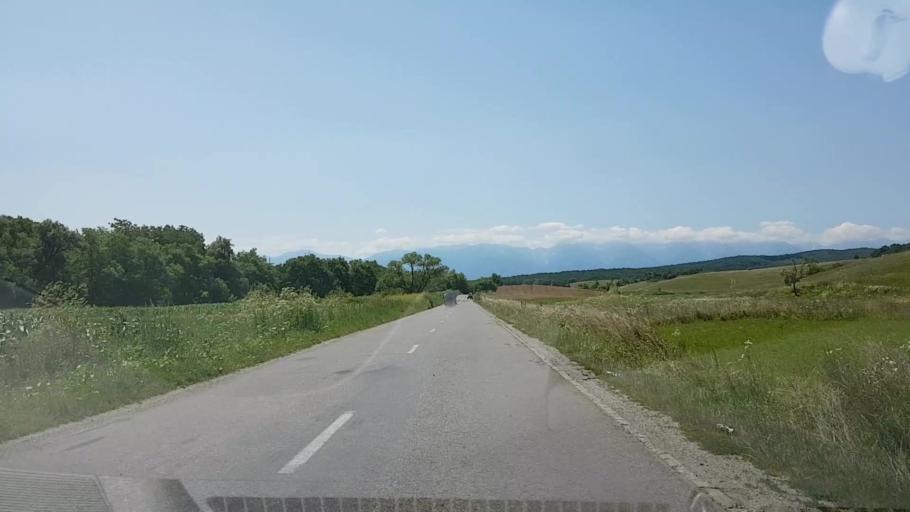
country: RO
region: Brasov
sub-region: Comuna Cincu
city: Cincu
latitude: 45.9012
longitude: 24.8119
